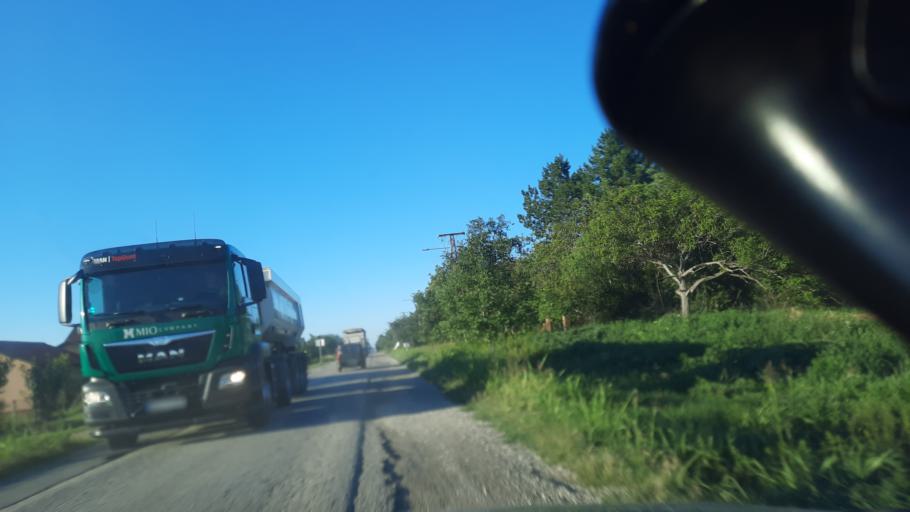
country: RS
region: Autonomna Pokrajina Vojvodina
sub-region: Sremski Okrug
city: Irig
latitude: 45.1110
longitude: 19.9325
